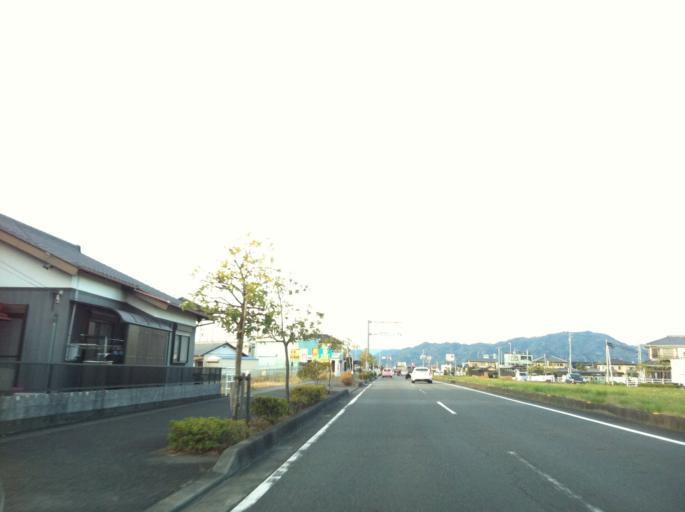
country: JP
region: Shizuoka
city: Yaizu
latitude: 34.8404
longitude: 138.3000
